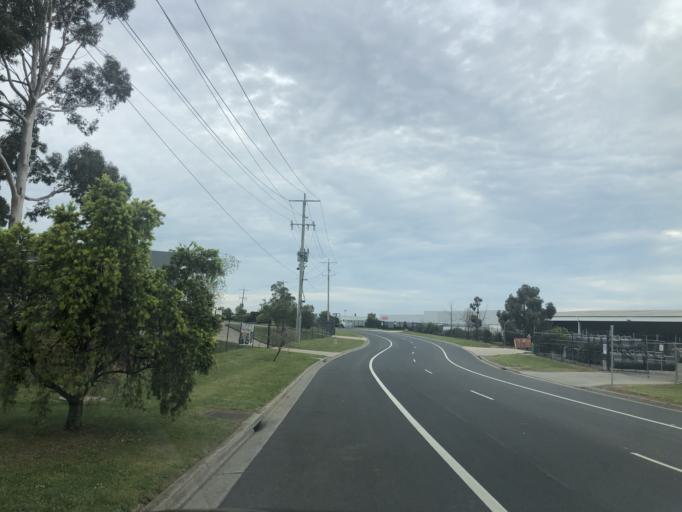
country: AU
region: Victoria
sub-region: Casey
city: Hallam
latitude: -38.0059
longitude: 145.2634
